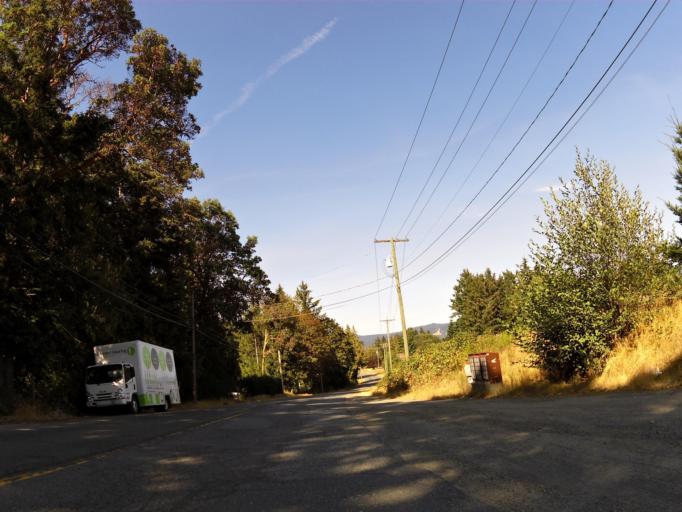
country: CA
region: British Columbia
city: North Saanich
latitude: 48.6743
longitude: -123.5522
